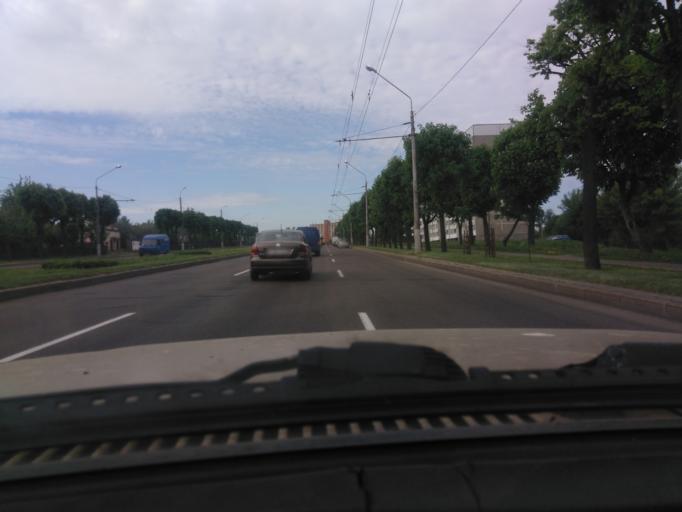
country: BY
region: Mogilev
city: Mahilyow
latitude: 53.9010
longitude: 30.2981
